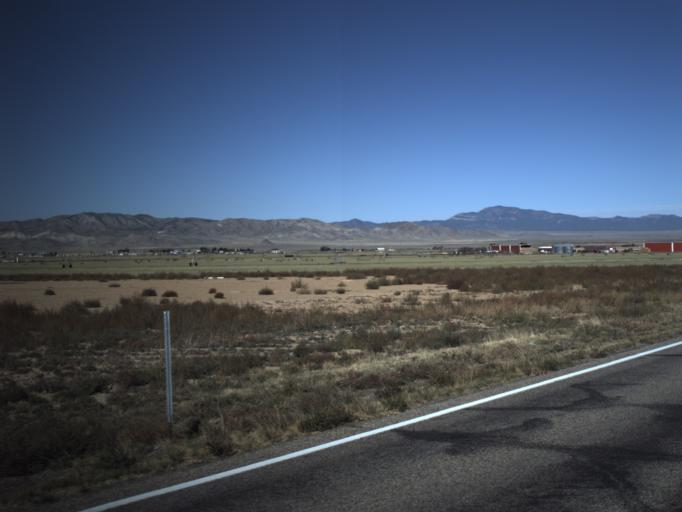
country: US
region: Utah
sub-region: Beaver County
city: Milford
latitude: 38.3463
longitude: -112.9813
